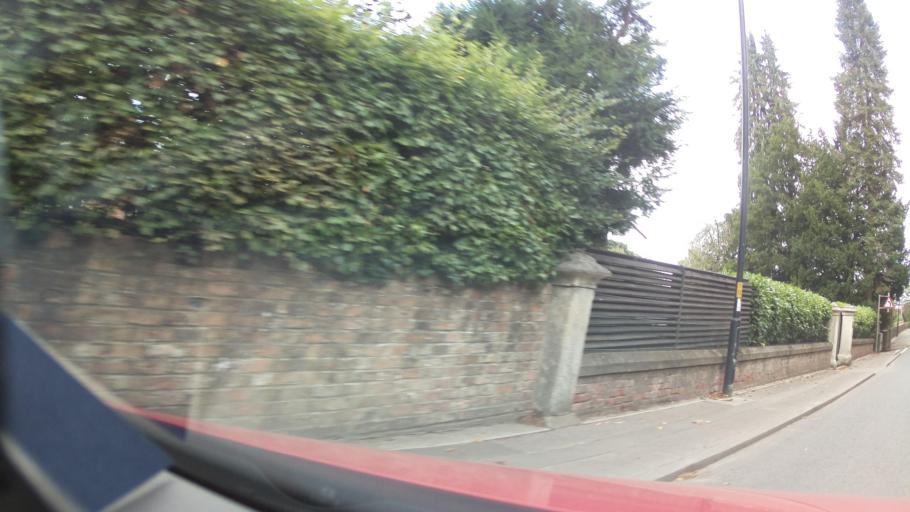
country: GB
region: England
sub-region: North Yorkshire
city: Ripon
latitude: 54.1439
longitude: -1.5270
